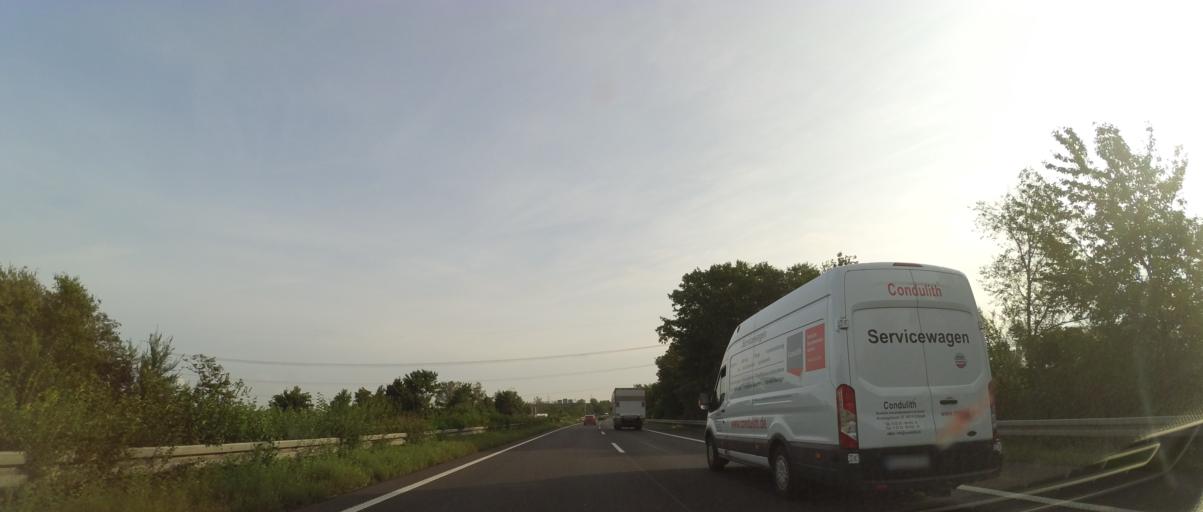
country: DE
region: North Rhine-Westphalia
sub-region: Regierungsbezirk Koln
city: Erftstadt
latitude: 50.8294
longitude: 6.7880
